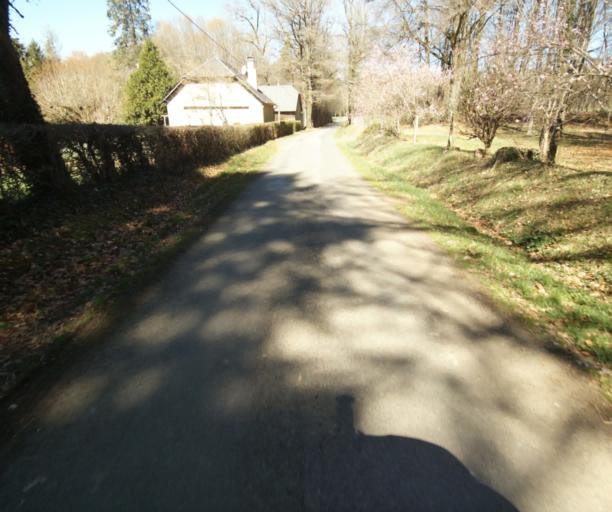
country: FR
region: Limousin
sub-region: Departement de la Correze
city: Chamboulive
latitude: 45.4168
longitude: 1.7294
